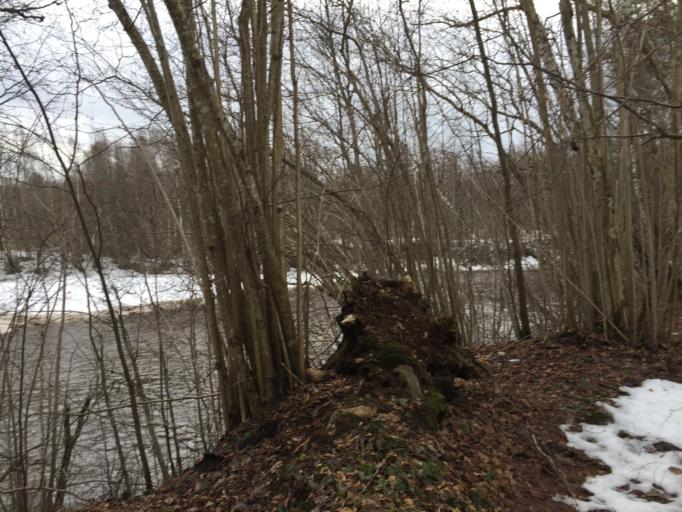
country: LV
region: Salacgrivas
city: Ainazi
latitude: 57.8533
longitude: 24.5176
